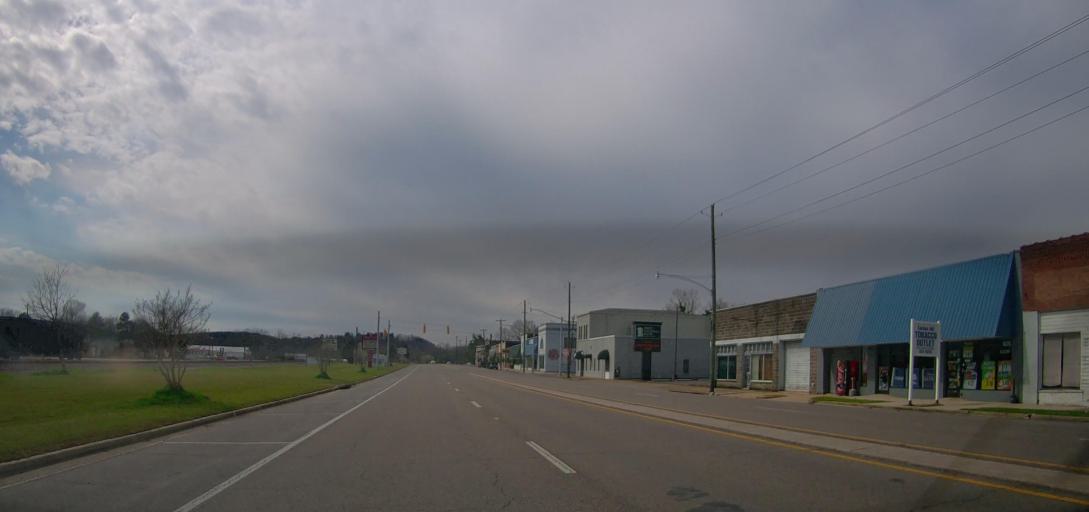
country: US
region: Alabama
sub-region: Walker County
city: Carbon Hill
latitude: 33.8884
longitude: -87.5287
